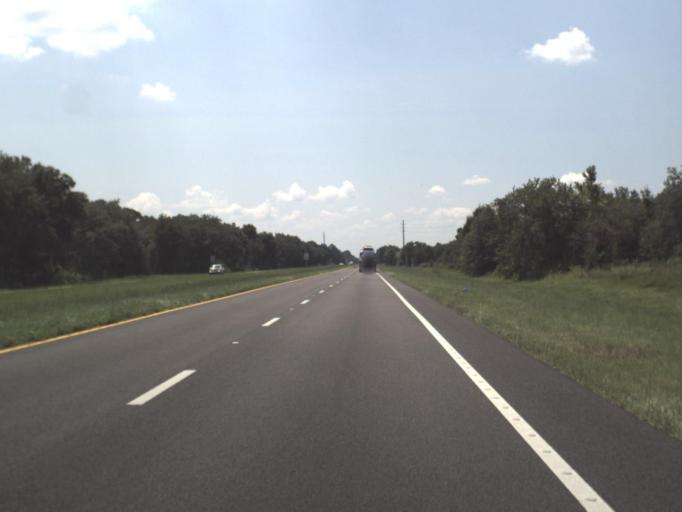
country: US
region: Florida
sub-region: Levy County
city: Inglis
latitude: 28.9999
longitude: -82.6550
